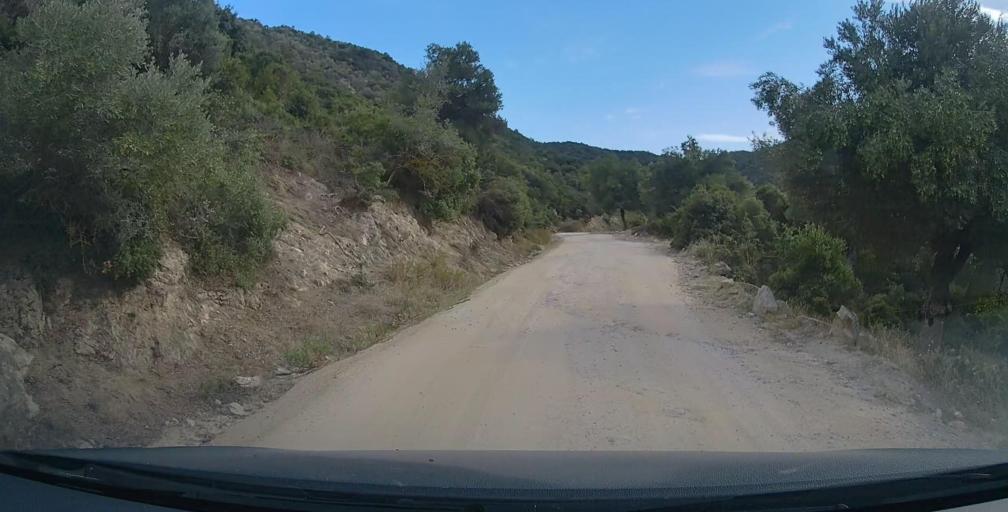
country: GR
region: Central Macedonia
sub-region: Nomos Chalkidikis
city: Sykia
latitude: 40.0162
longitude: 23.9387
